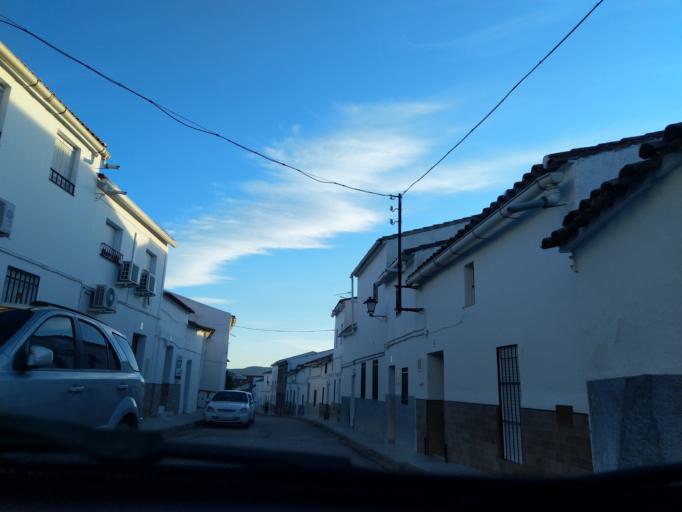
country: ES
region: Extremadura
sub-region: Provincia de Badajoz
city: Valverde de Llerena
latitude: 38.2158
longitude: -5.8220
